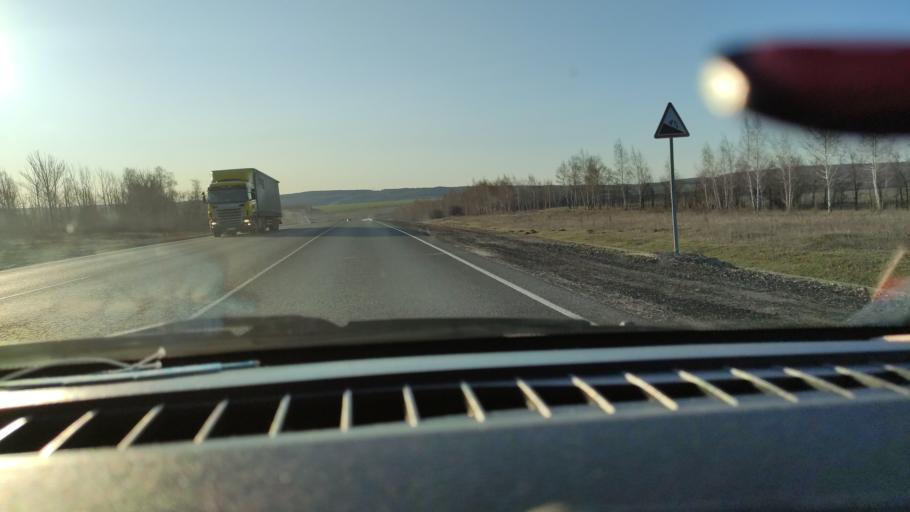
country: RU
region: Saratov
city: Shikhany
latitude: 52.1211
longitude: 47.2620
